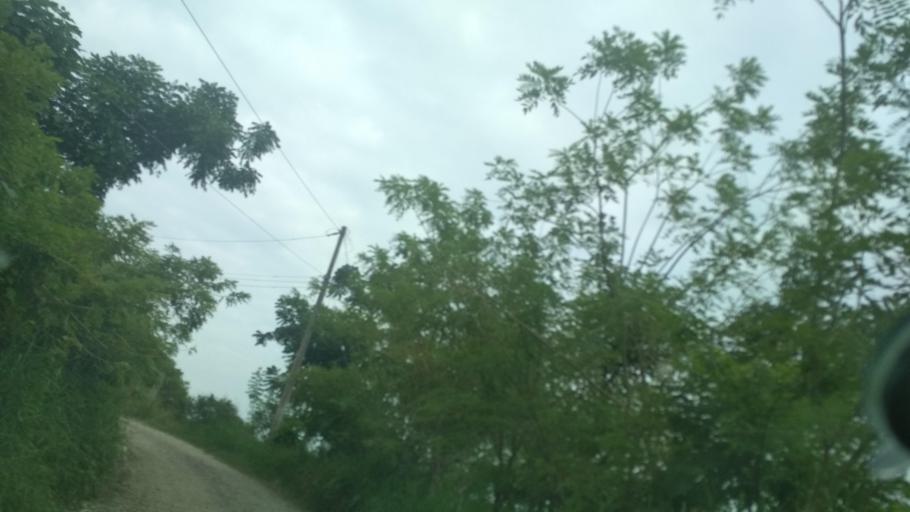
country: MX
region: Veracruz
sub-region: Poza Rica de Hidalgo
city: El Mollejon
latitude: 20.5216
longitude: -97.3793
